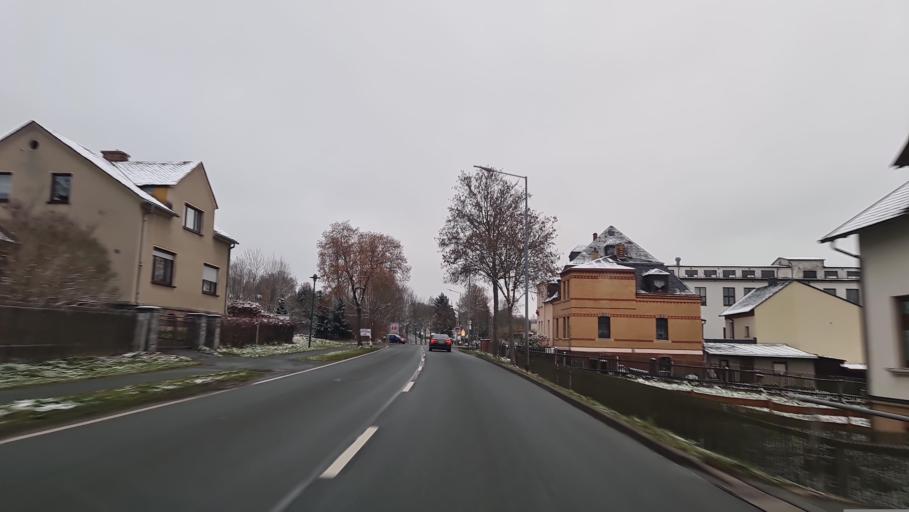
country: DE
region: Saxony
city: Adorf
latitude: 50.3173
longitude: 12.2749
